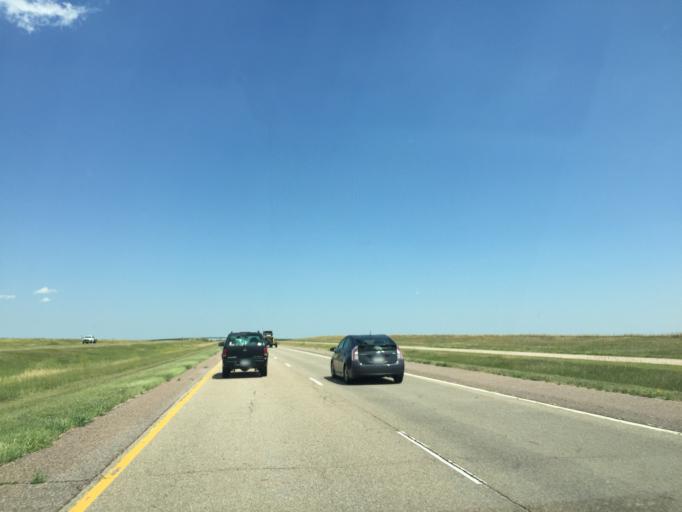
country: US
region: Colorado
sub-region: Lincoln County
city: Hugo
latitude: 39.2803
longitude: -103.3611
